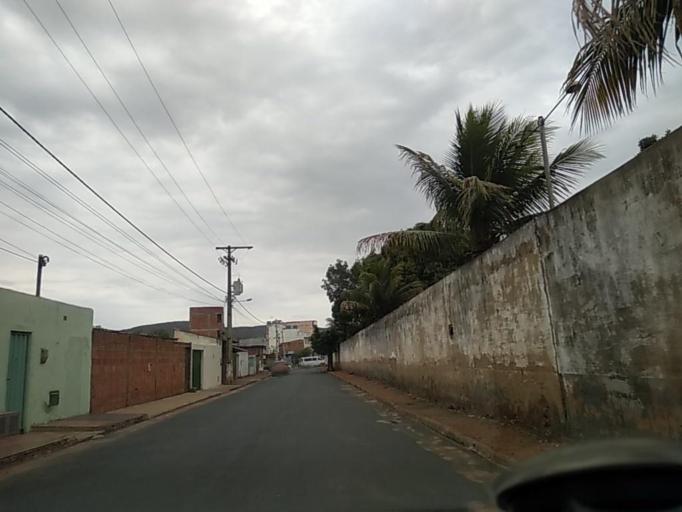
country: BR
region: Bahia
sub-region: Caetite
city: Caetite
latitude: -14.0572
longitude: -42.4827
